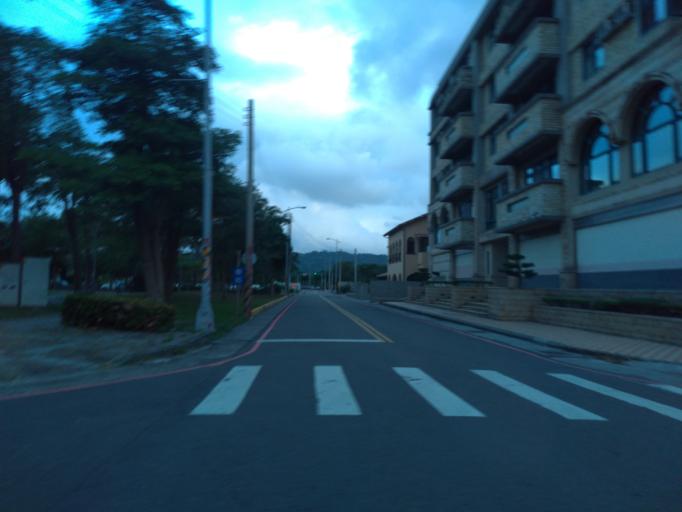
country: TW
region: Taiwan
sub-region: Hsinchu
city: Zhubei
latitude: 24.8040
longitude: 121.0411
